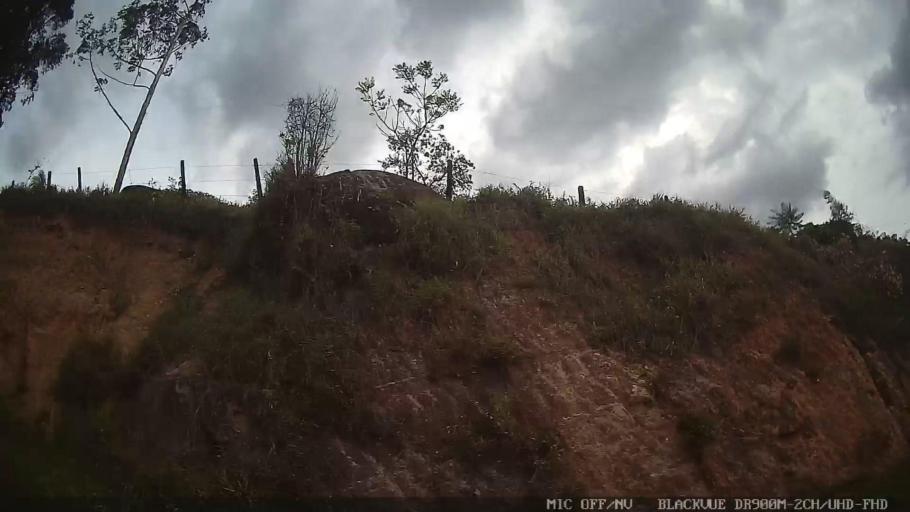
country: BR
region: Sao Paulo
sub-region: Amparo
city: Amparo
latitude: -22.8267
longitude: -46.7665
